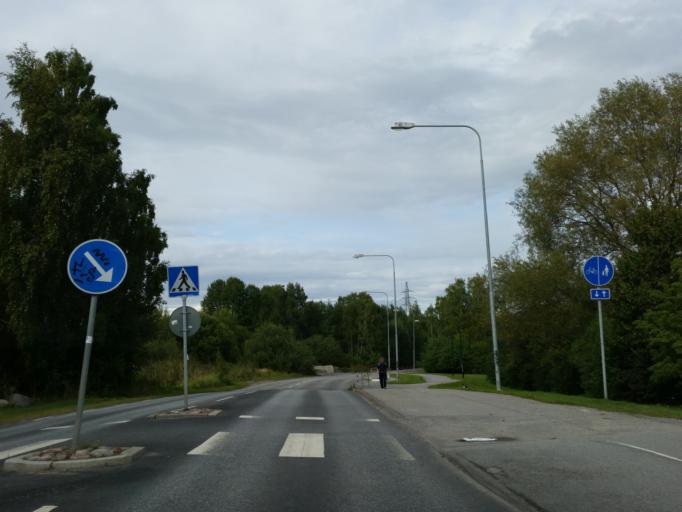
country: SE
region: Stockholm
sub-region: Solna Kommun
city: Rasunda
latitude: 59.3736
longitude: 17.9820
